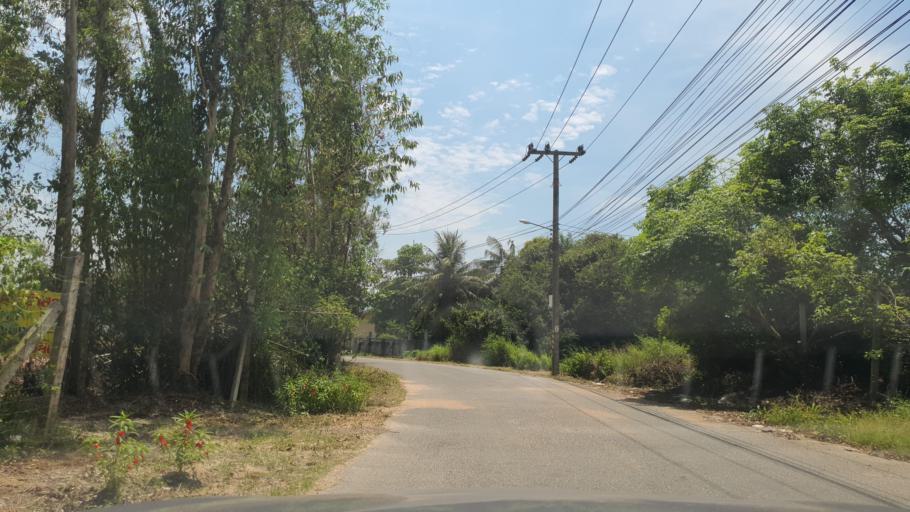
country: TH
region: Rayong
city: Ban Chang
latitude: 12.8006
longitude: 100.9466
